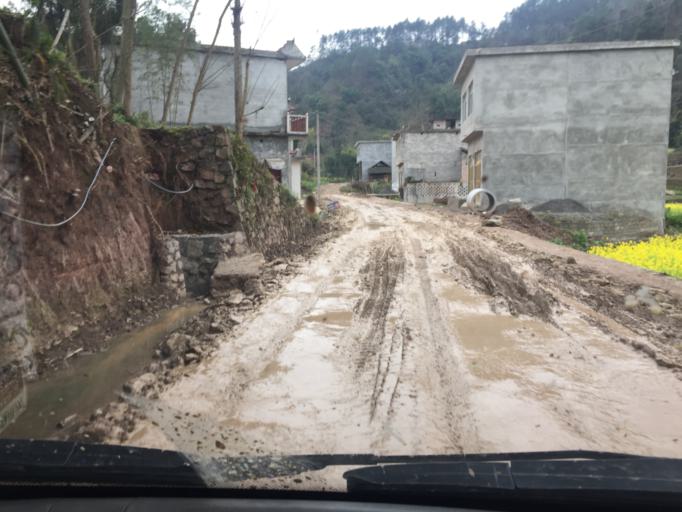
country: CN
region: Guizhou Sheng
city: Fuxing
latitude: 28.0548
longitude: 107.9072
